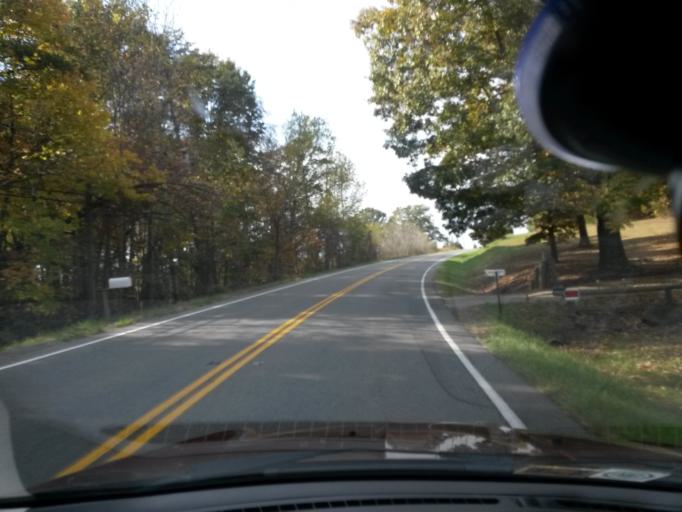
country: US
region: Virginia
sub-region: Franklin County
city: North Shore
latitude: 37.1147
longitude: -79.8019
